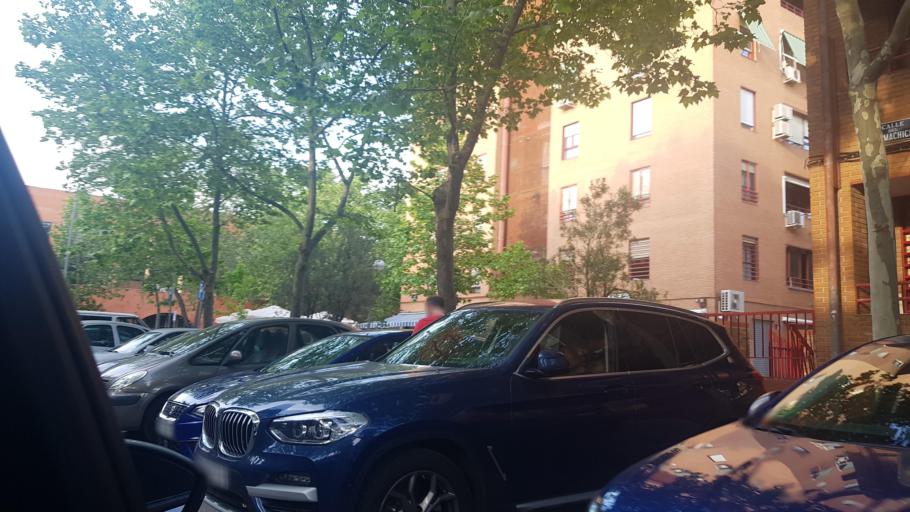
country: ES
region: Madrid
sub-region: Provincia de Madrid
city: Puente de Vallecas
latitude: 40.3730
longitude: -3.6606
